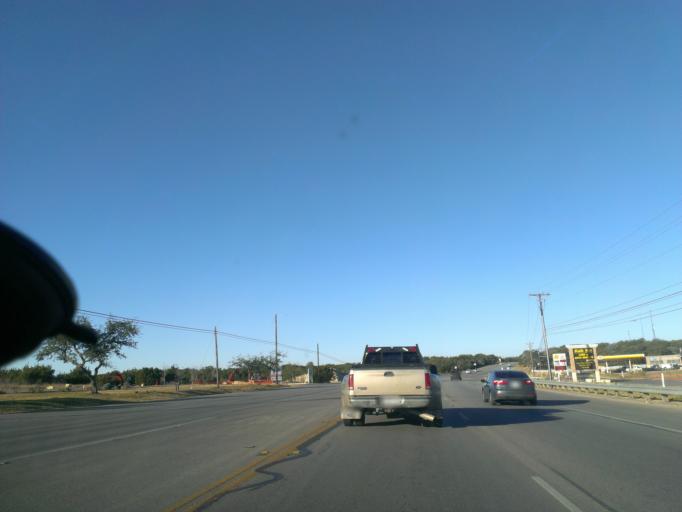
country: US
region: Texas
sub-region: Hays County
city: Dripping Springs
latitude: 30.1967
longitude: -97.9978
